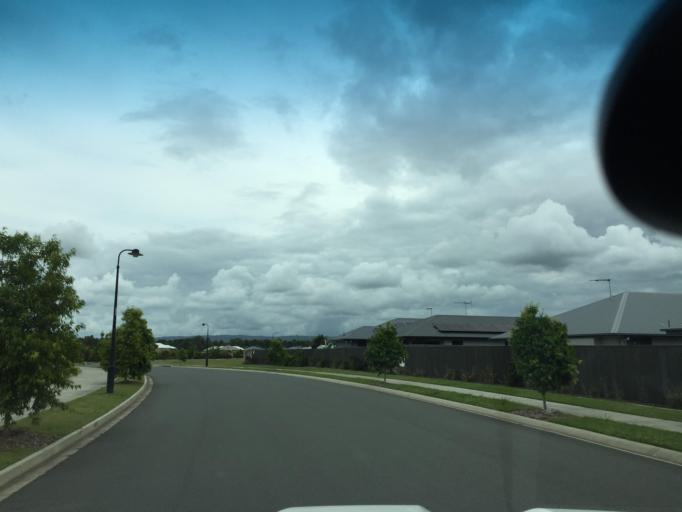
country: AU
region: Queensland
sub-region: Moreton Bay
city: Caboolture
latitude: -27.0627
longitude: 152.9290
